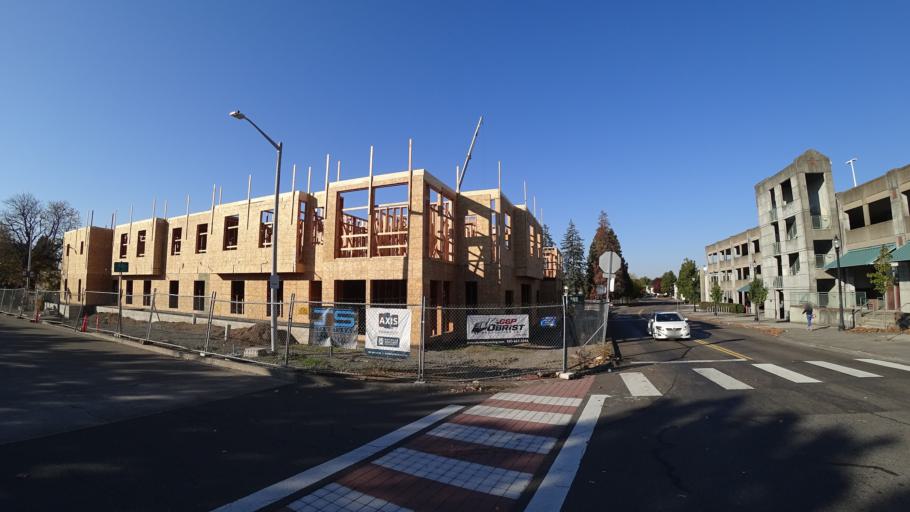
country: US
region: Oregon
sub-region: Multnomah County
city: Gresham
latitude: 45.5029
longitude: -122.4263
